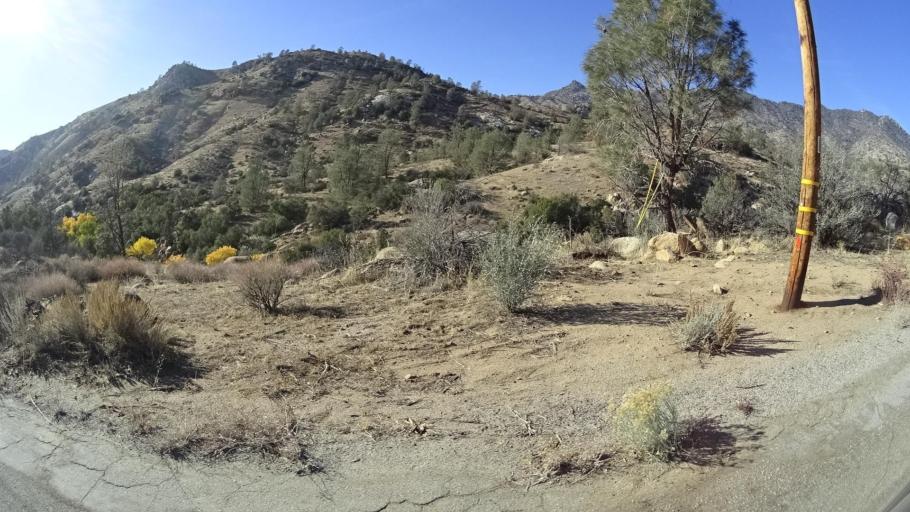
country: US
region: California
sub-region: Kern County
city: Weldon
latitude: 35.7229
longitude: -118.3040
